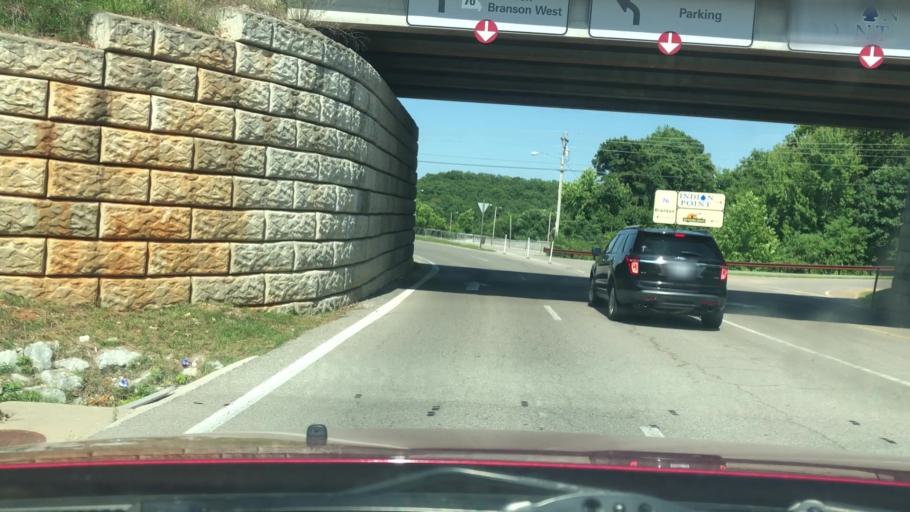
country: US
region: Missouri
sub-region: Stone County
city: Kimberling City
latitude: 36.6605
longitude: -93.3374
